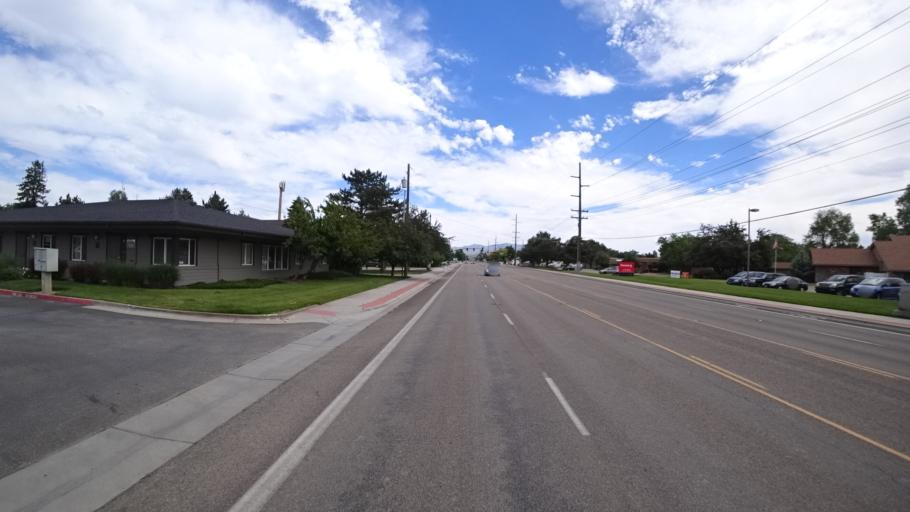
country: US
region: Idaho
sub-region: Ada County
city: Garden City
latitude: 43.6340
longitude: -116.2862
